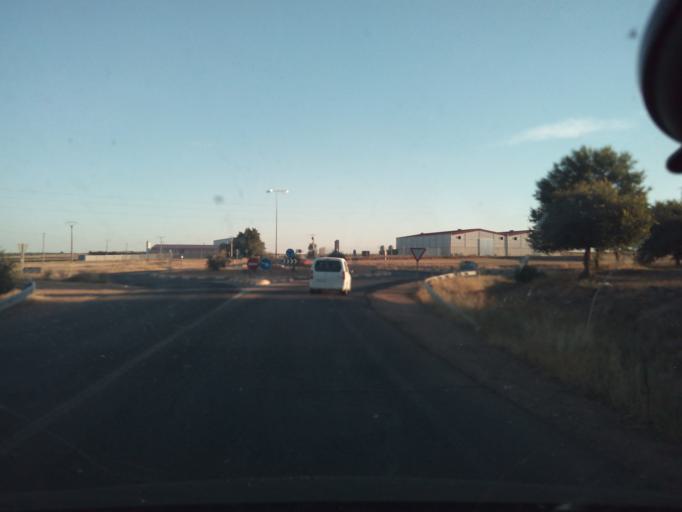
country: ES
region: Castille-La Mancha
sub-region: Province of Toledo
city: Villacanas
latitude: 39.6106
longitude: -3.3377
